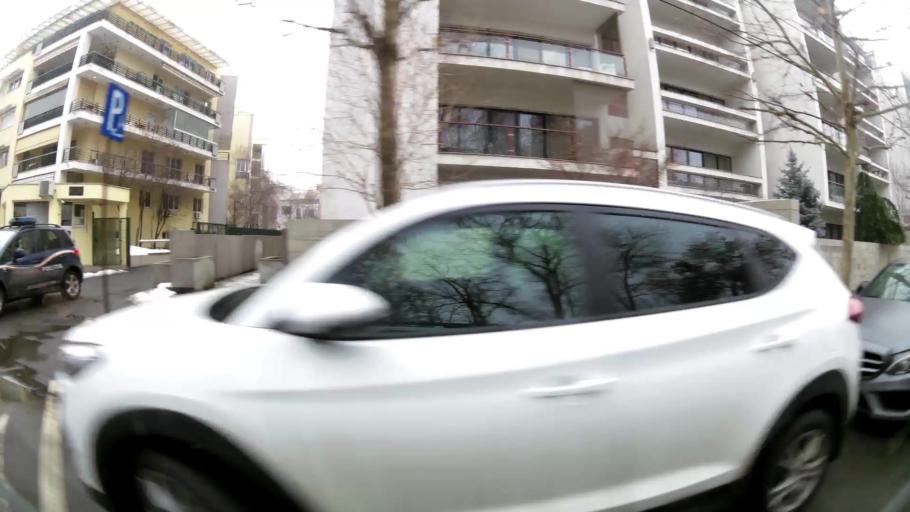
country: RO
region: Bucuresti
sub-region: Municipiul Bucuresti
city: Bucharest
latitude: 44.4808
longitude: 26.0862
